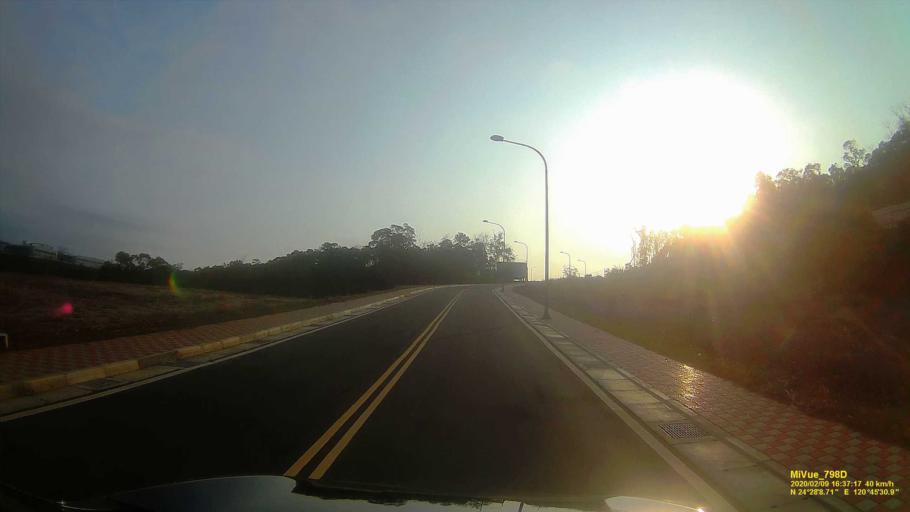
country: TW
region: Taiwan
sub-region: Miaoli
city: Miaoli
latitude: 24.4690
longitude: 120.7585
